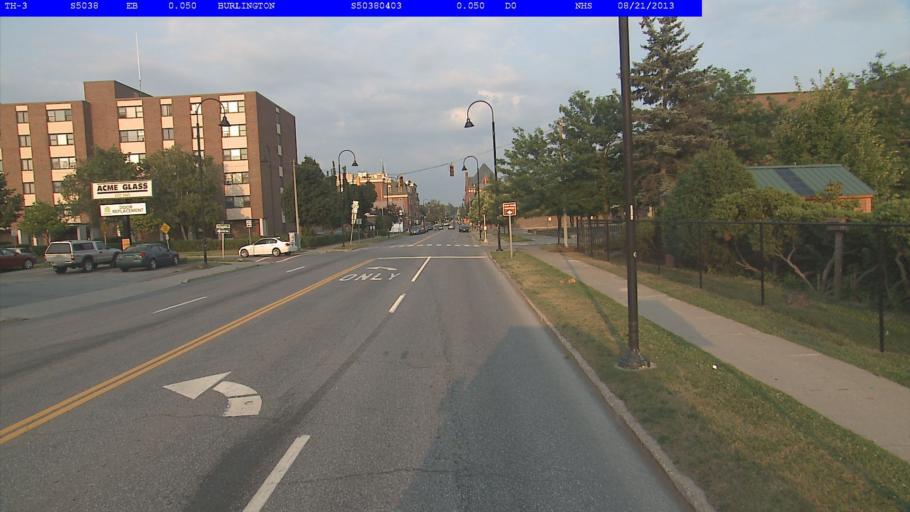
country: US
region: Vermont
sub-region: Chittenden County
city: Burlington
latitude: 44.4802
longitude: -73.2180
